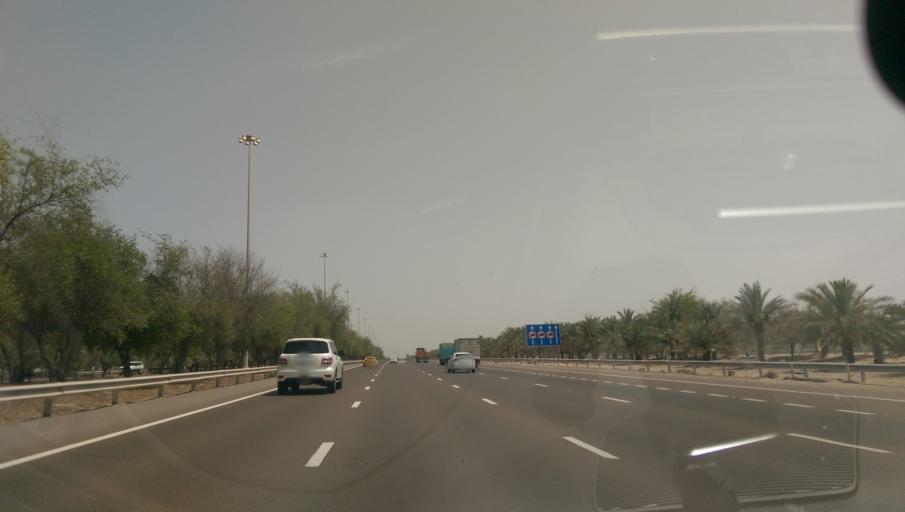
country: AE
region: Abu Dhabi
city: Abu Dhabi
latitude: 24.4711
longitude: 54.6766
